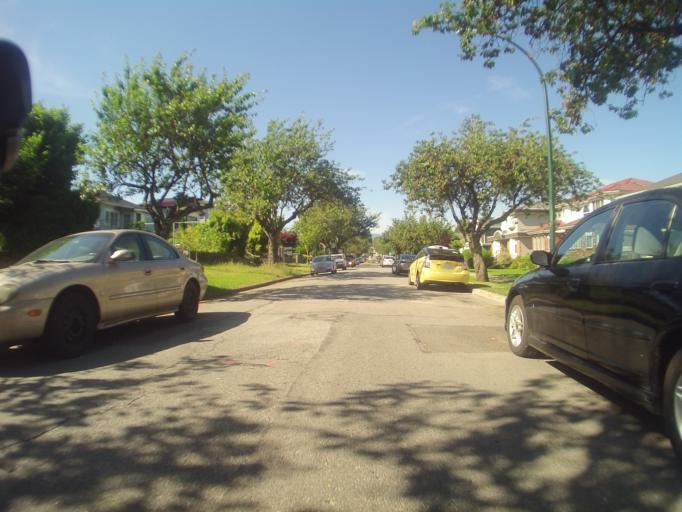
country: CA
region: British Columbia
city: Vancouver
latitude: 49.2300
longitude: -123.0799
